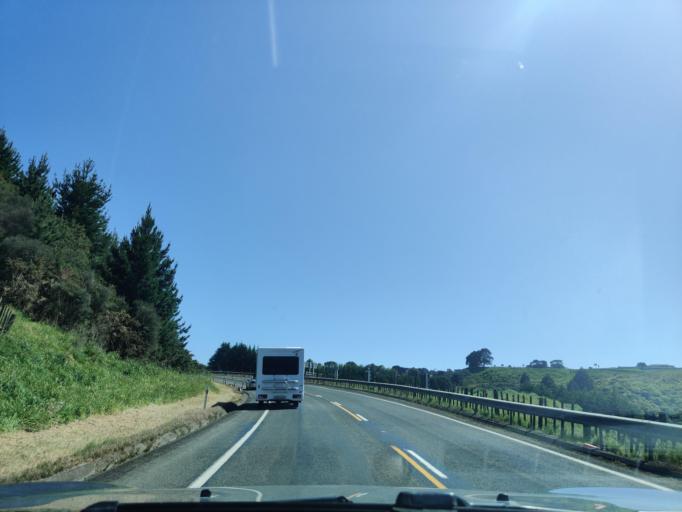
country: NZ
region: Manawatu-Wanganui
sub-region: Wanganui District
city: Wanganui
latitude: -39.8436
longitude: 174.9241
